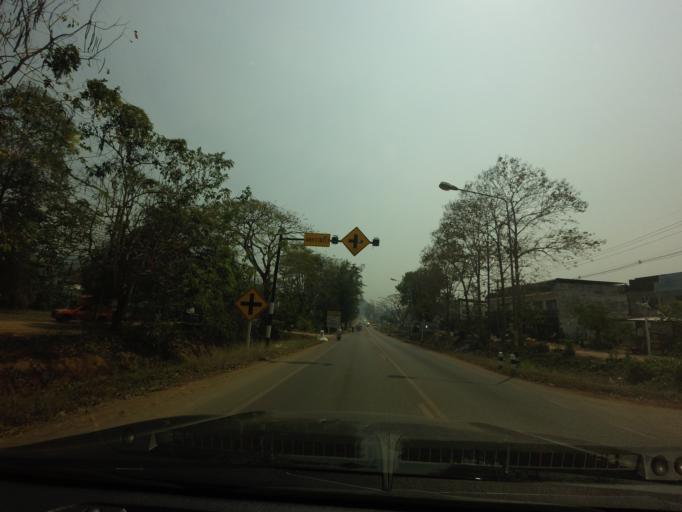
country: TH
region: Kanchanaburi
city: Thong Pha Phum
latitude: 14.7390
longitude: 98.6311
